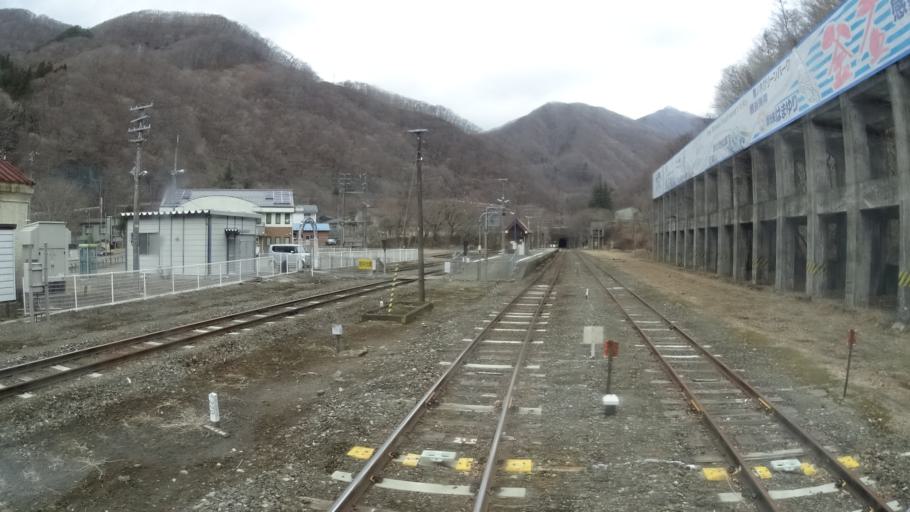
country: JP
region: Iwate
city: Kamaishi
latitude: 39.2799
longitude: 141.7189
